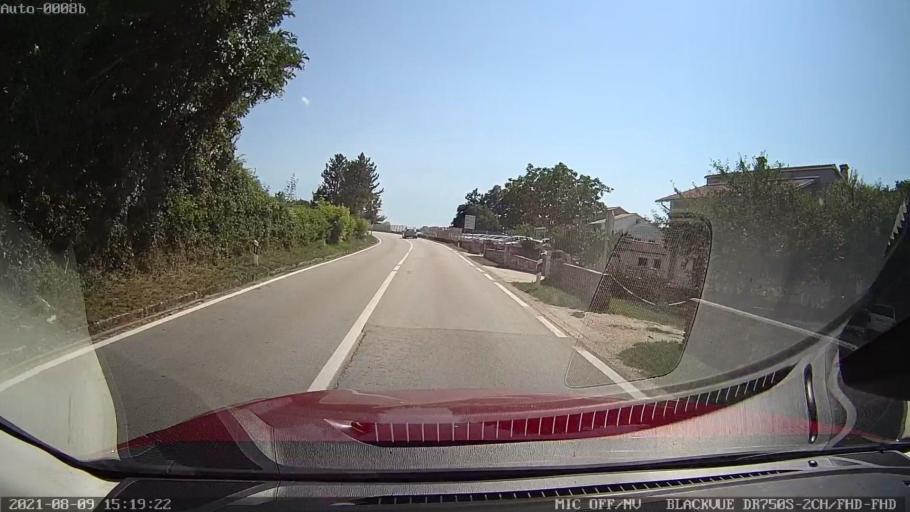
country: HR
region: Istarska
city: Pazin
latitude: 45.2154
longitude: 13.9017
